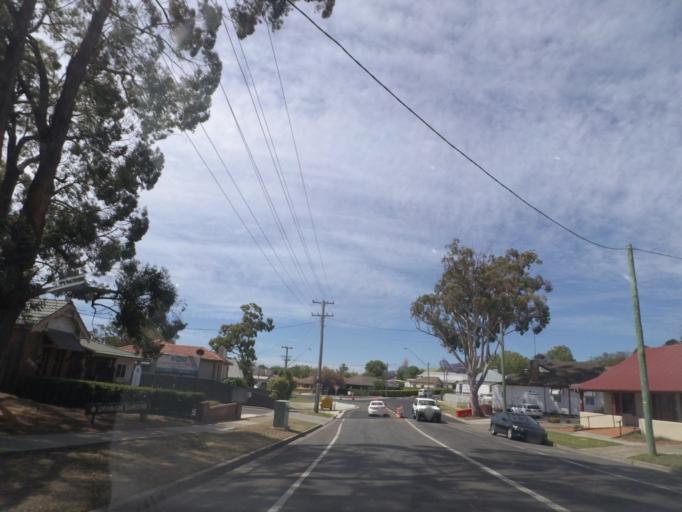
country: AU
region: New South Wales
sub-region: Camden
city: Elderslie
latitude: -34.0578
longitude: 150.6941
